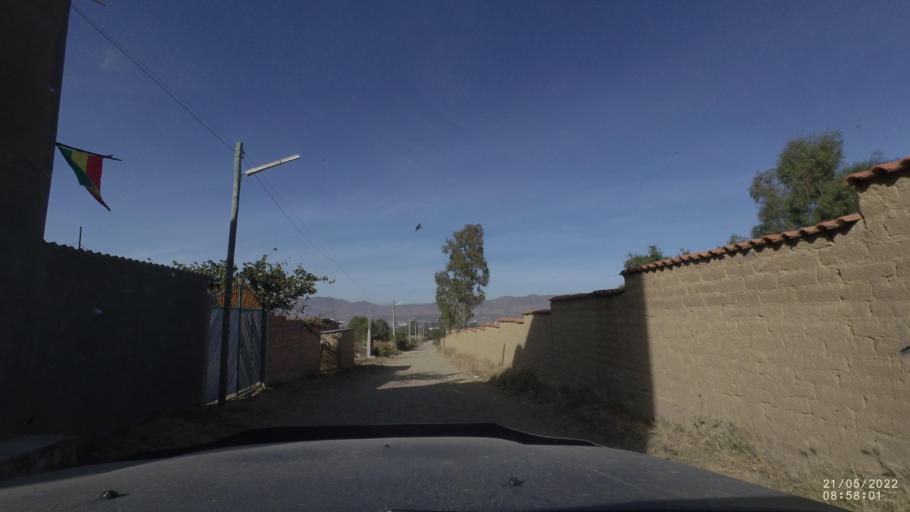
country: BO
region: Cochabamba
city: Cochabamba
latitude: -17.3791
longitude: -66.0384
